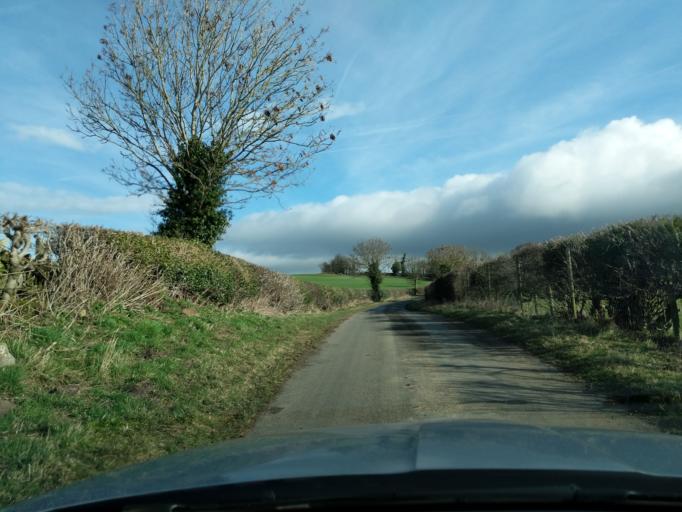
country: GB
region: England
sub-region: North Yorkshire
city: Catterick Garrison
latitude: 54.3403
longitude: -1.6944
